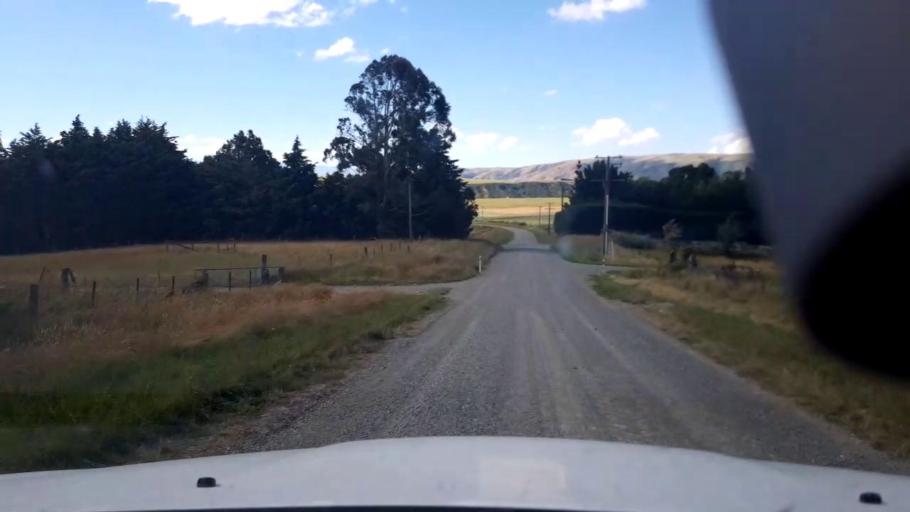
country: NZ
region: Canterbury
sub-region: Timaru District
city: Pleasant Point
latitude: -44.3065
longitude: 170.8730
